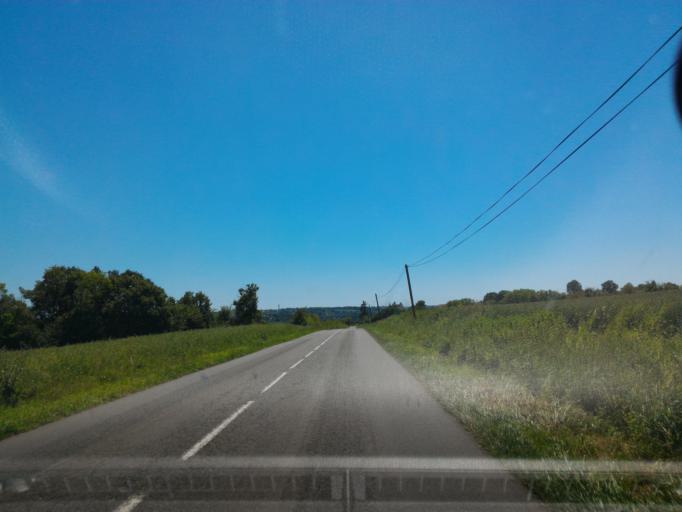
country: FR
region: Poitou-Charentes
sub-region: Departement de la Vienne
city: Availles-Limouzine
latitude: 46.2559
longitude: 0.6647
